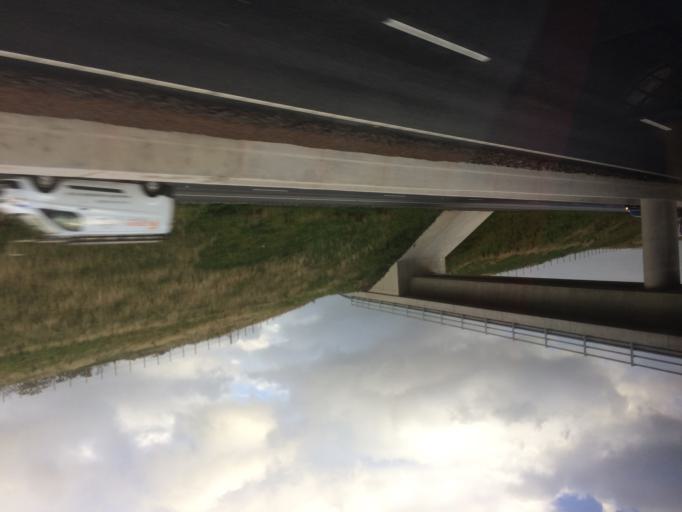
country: GB
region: Scotland
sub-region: North Lanarkshire
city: Coatbridge
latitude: 55.8400
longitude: -4.0395
